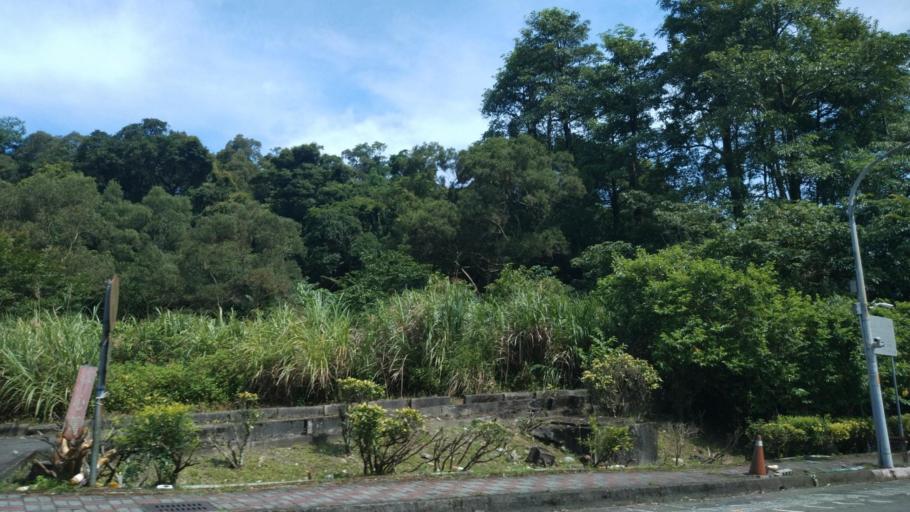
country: TW
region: Taipei
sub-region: Taipei
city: Banqiao
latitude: 24.9530
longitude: 121.5090
